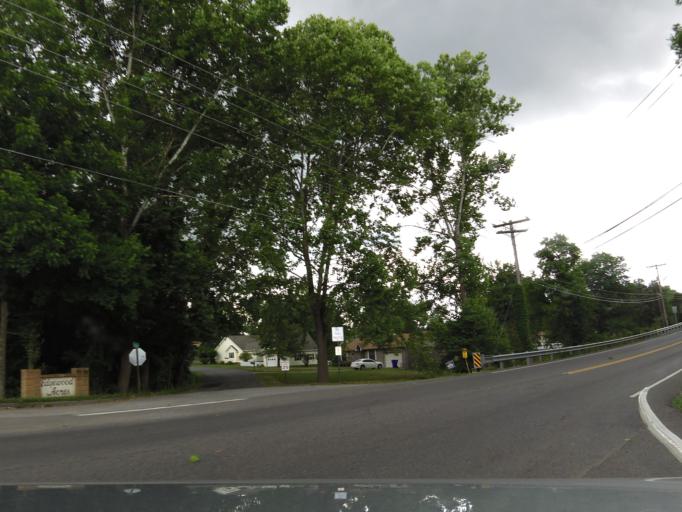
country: US
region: Tennessee
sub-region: Blount County
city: Eagleton Village
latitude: 35.8093
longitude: -83.9381
